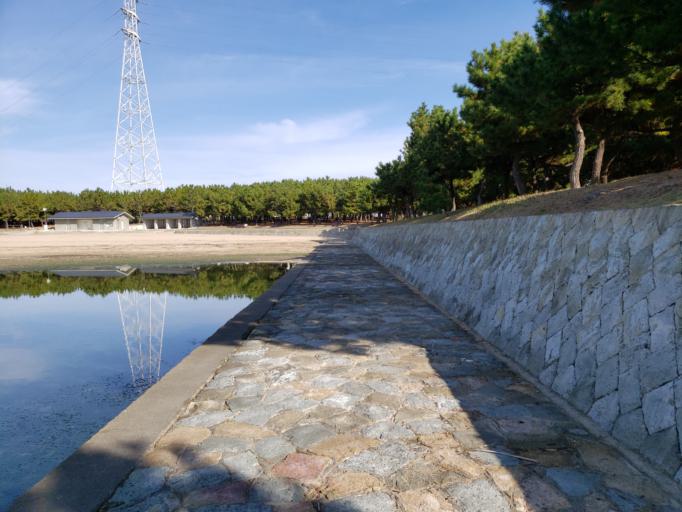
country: JP
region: Hyogo
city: Kakogawacho-honmachi
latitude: 34.7330
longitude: 134.8035
